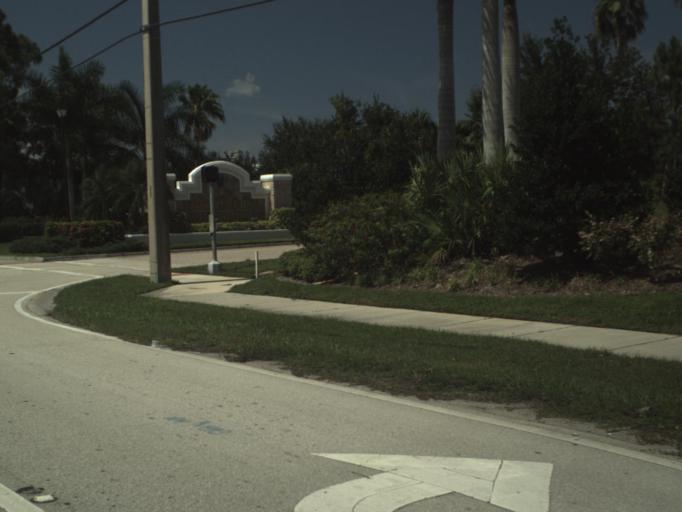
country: US
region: Florida
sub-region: Martin County
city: North River Shores
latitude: 27.2287
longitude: -80.2658
